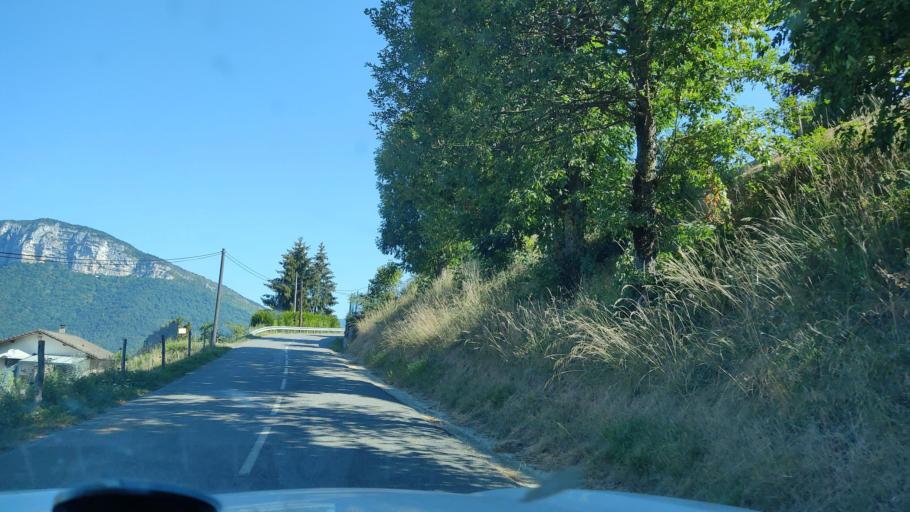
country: FR
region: Rhone-Alpes
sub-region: Departement de la Savoie
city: Barby
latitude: 45.5705
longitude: 6.0264
